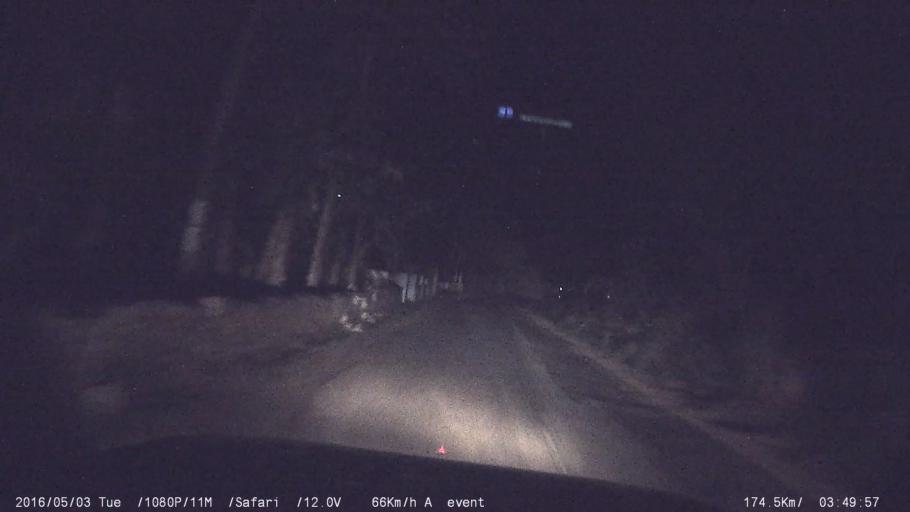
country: IN
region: Kerala
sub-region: Kottayam
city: Palackattumala
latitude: 9.8247
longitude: 76.6075
